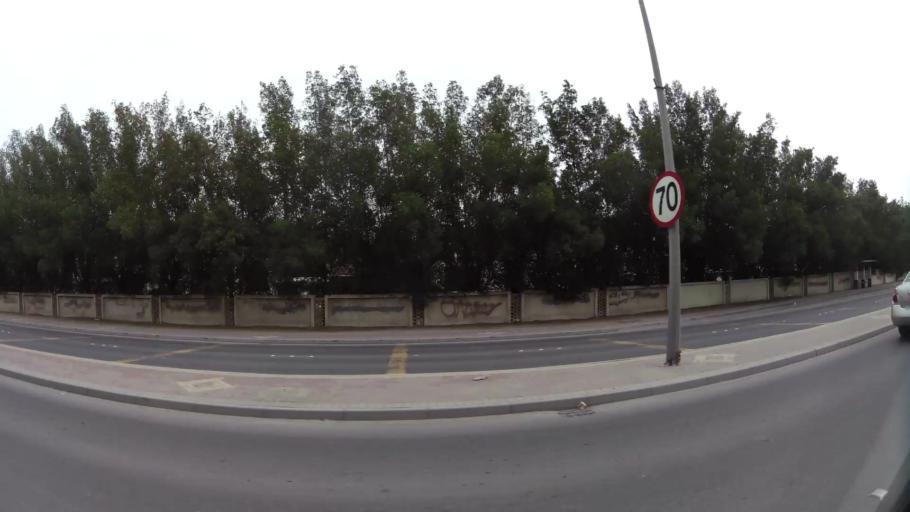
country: BH
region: Manama
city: Jidd Hafs
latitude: 26.2064
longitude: 50.5339
